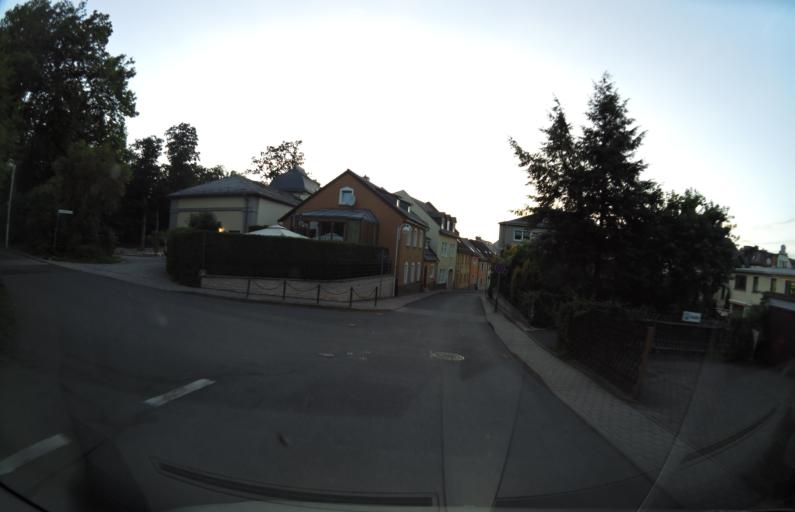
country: DE
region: Thuringia
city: Schleiz
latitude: 50.5764
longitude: 11.8152
